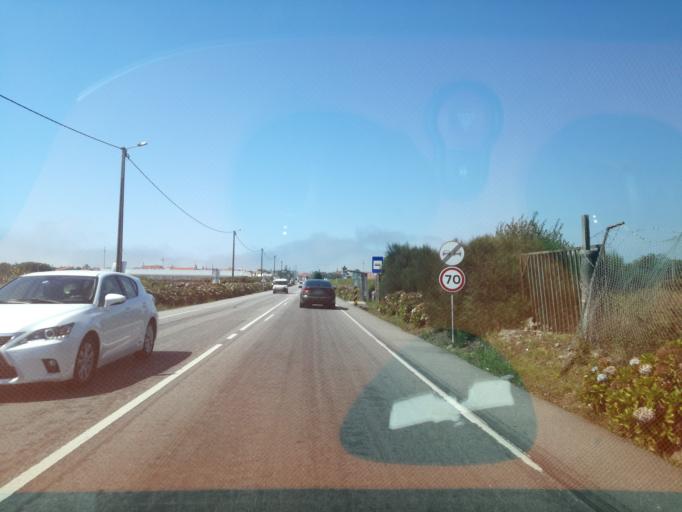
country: PT
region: Braga
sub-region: Esposende
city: Apulia
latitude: 41.5052
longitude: -8.7633
